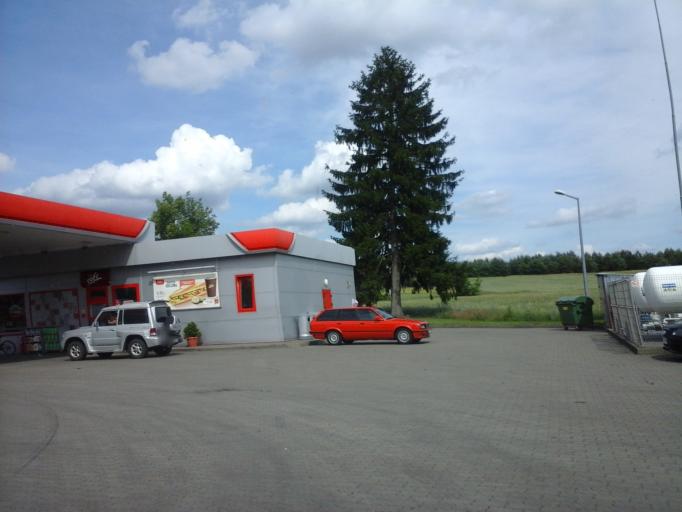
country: PL
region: West Pomeranian Voivodeship
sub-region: Powiat lobeski
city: Lobez
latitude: 53.6219
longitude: 15.6126
